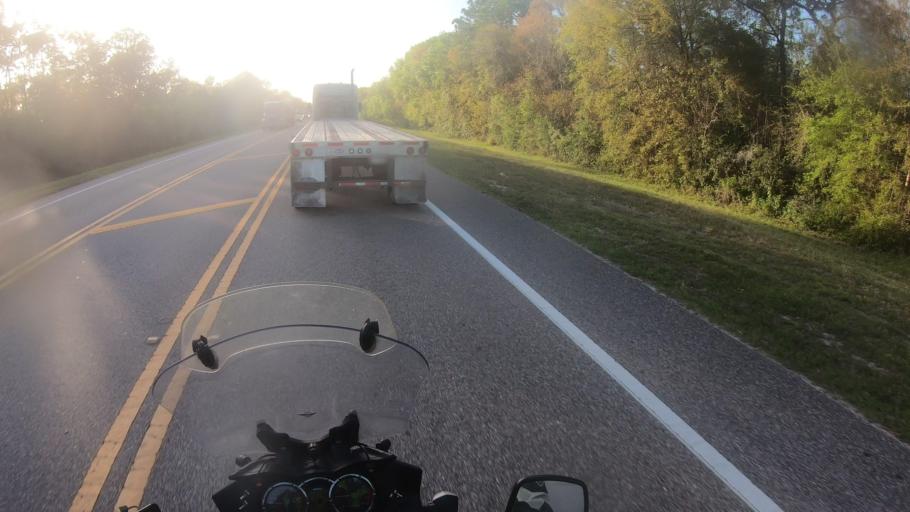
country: US
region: Florida
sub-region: Sarasota County
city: The Meadows
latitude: 27.4147
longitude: -82.3439
